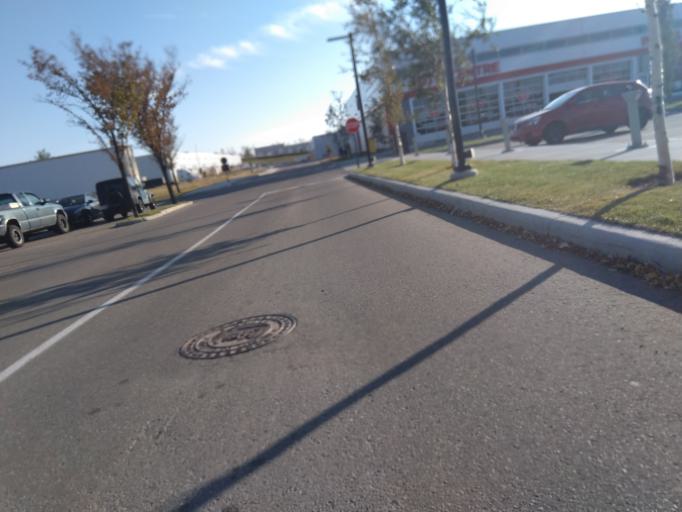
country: CA
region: Alberta
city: Calgary
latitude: 51.1069
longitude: -114.0413
